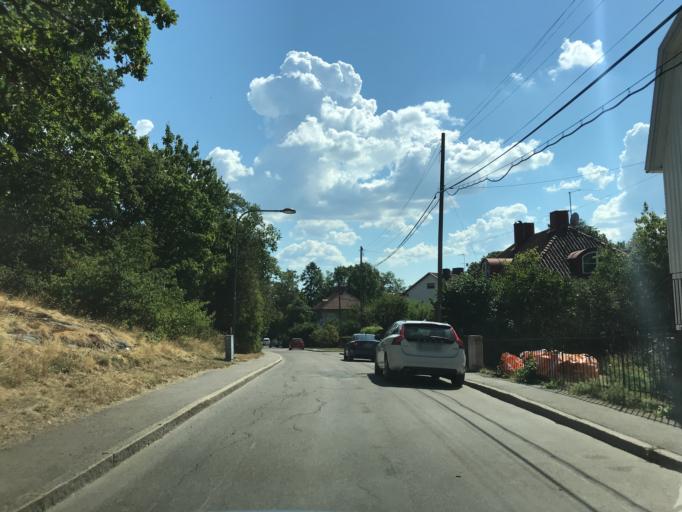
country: SE
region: Stockholm
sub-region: Solna Kommun
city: Solna
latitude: 59.3206
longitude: 17.9926
